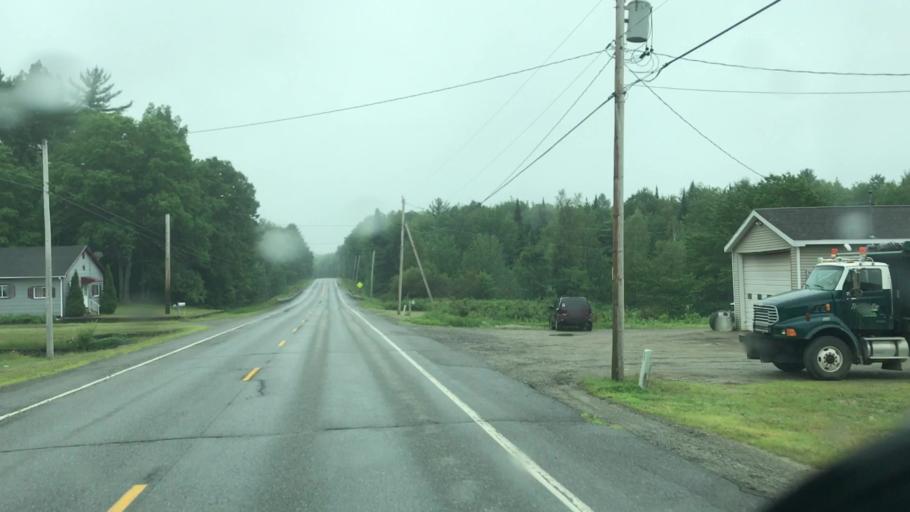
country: US
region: Maine
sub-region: Penobscot County
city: Howland
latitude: 45.2771
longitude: -68.6335
